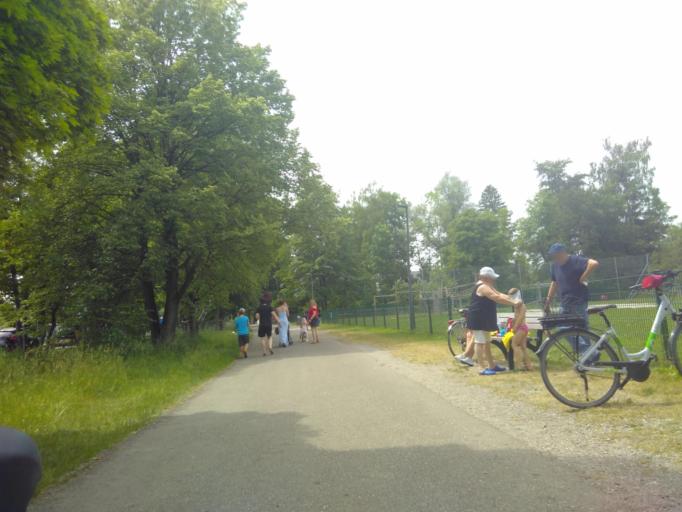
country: DE
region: Bavaria
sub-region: Upper Bavaria
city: Eichenau
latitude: 48.1766
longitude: 11.3201
